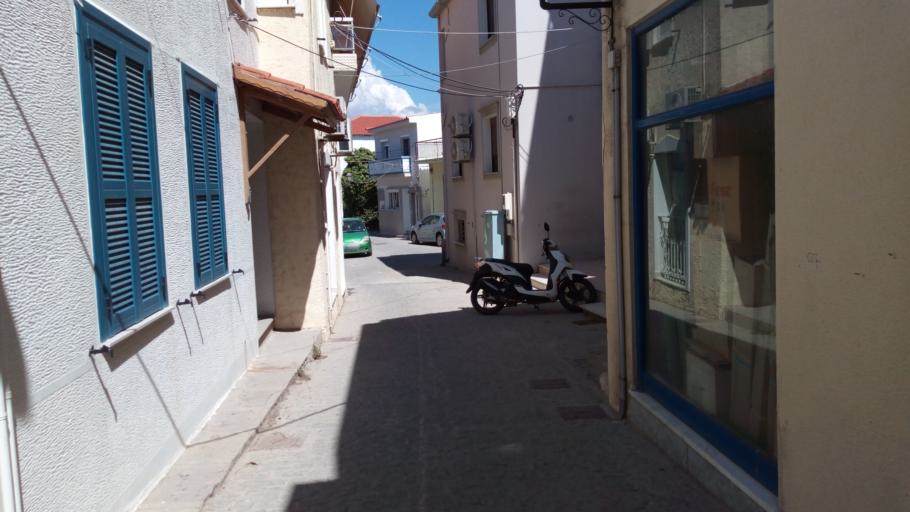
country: GR
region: North Aegean
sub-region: Nomos Lesvou
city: Myrina
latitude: 39.8764
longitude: 25.0600
